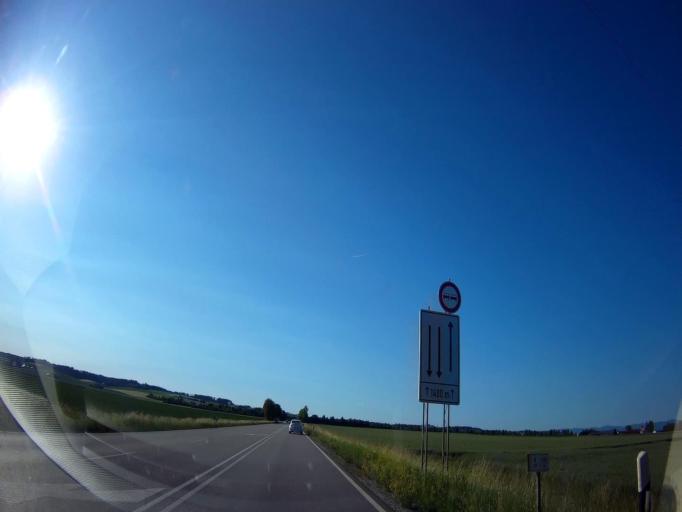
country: DE
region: Bavaria
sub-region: Lower Bavaria
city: Pilsting
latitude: 48.7213
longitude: 12.6670
